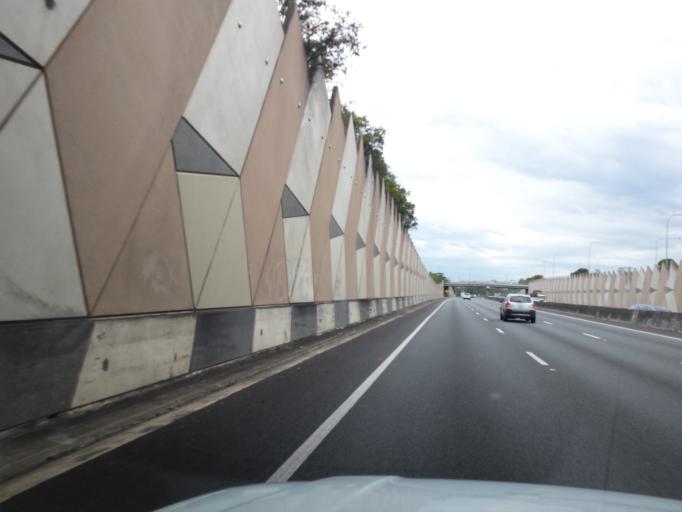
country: AU
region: Queensland
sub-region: Gold Coast
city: Nerang
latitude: -27.9936
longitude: 153.3402
